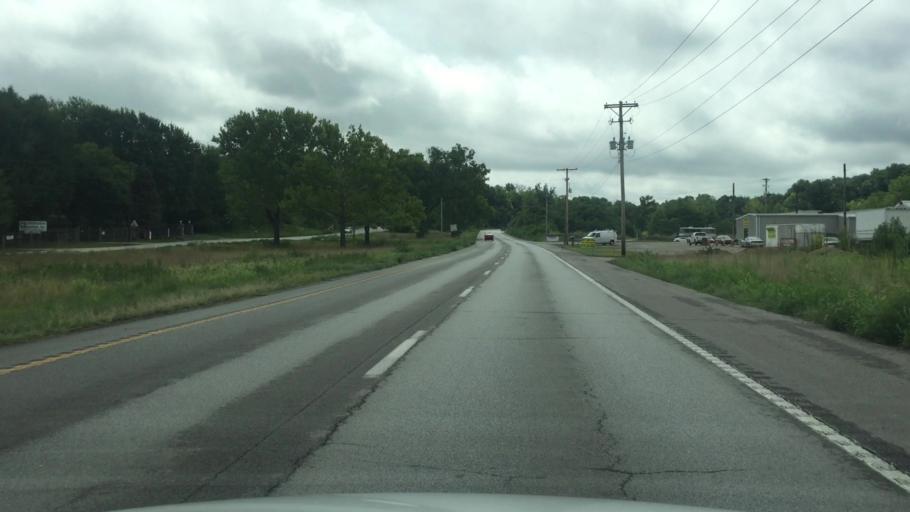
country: US
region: Missouri
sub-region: Jackson County
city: Raytown
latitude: 38.9609
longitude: -94.4245
